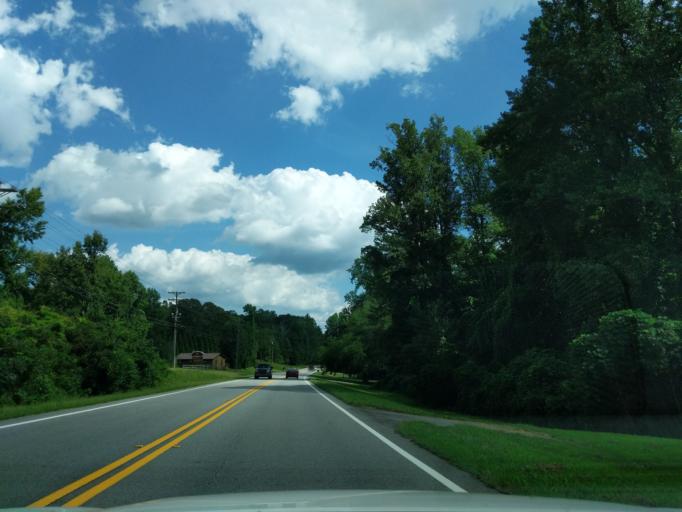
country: US
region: Georgia
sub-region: White County
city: Cleveland
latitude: 34.6239
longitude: -83.8042
